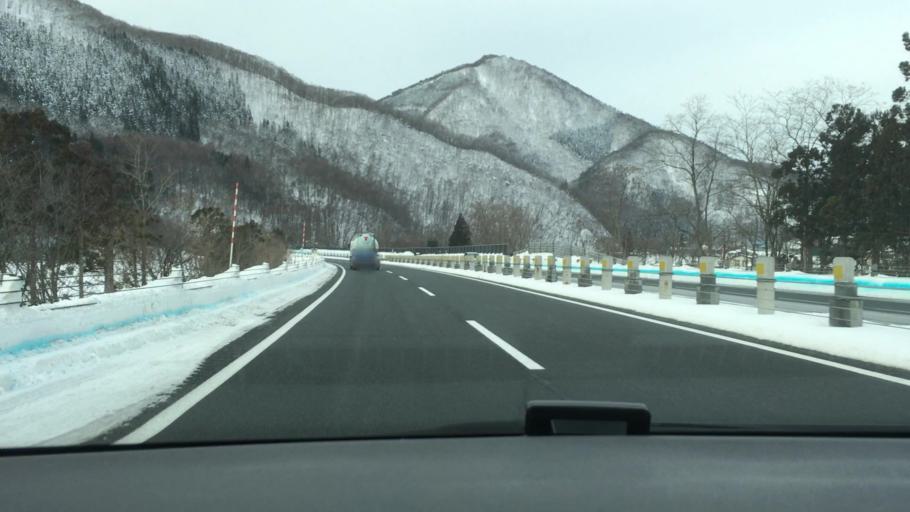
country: JP
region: Akita
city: Hanawa
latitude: 40.1364
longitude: 140.9475
